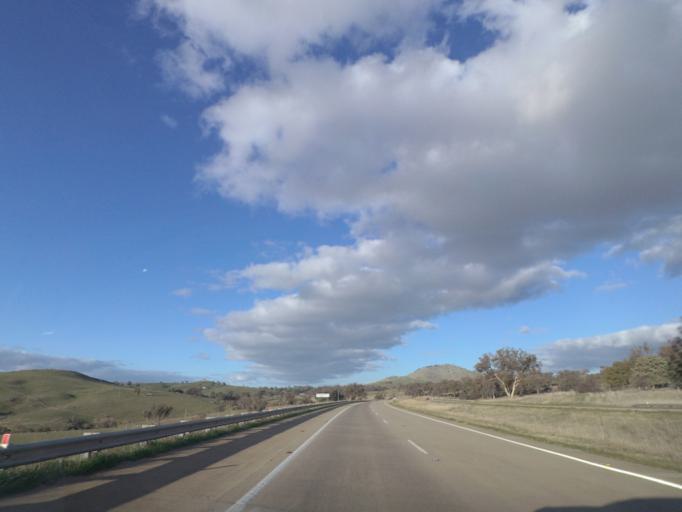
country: AU
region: New South Wales
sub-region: Gundagai
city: Gundagai
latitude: -34.8102
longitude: 148.4560
